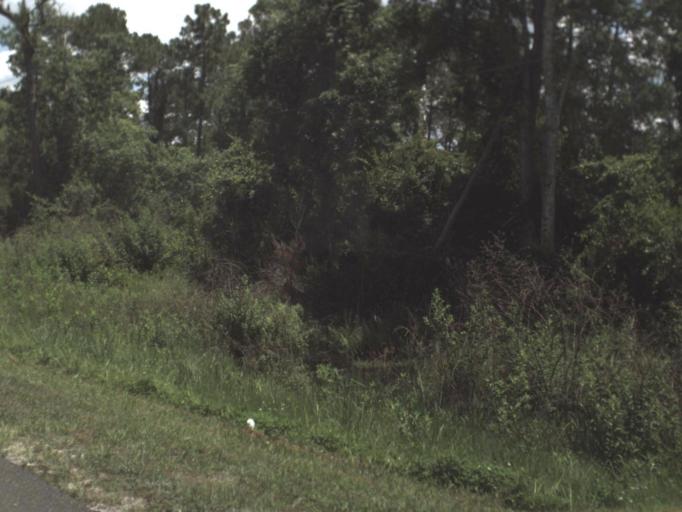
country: US
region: Florida
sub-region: Clay County
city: Keystone Heights
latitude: 29.7228
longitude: -82.0462
